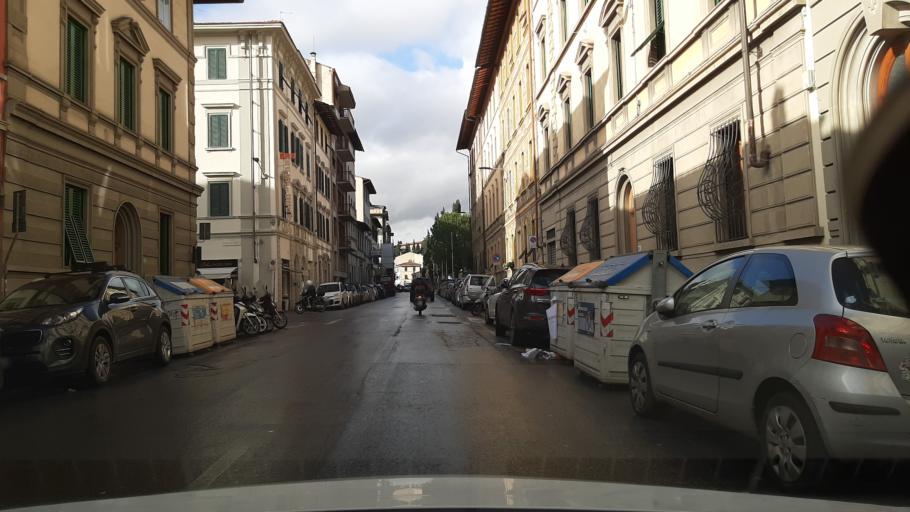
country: IT
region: Tuscany
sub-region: Province of Florence
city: Florence
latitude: 43.7906
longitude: 11.2545
